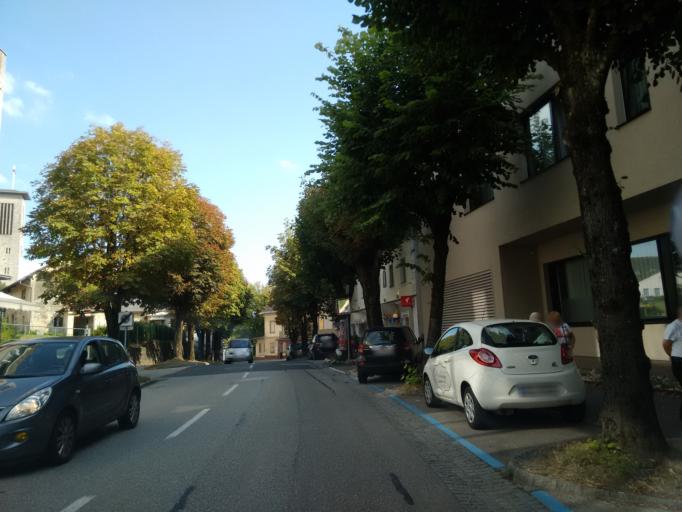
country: AT
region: Upper Austria
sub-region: Politischer Bezirk Grieskirchen
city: Bad Schallerbach
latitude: 48.2294
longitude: 13.9236
